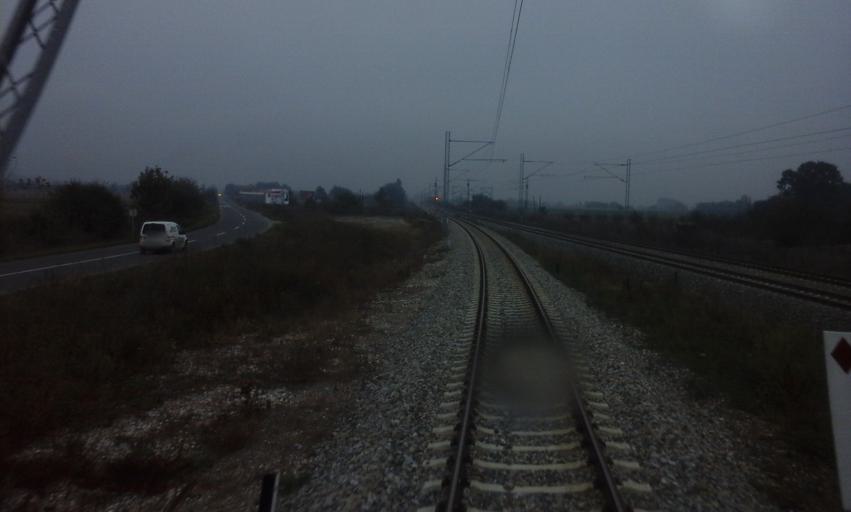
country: RS
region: Central Serbia
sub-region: Pomoravski Okrug
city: Paracin
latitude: 43.8856
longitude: 21.3838
